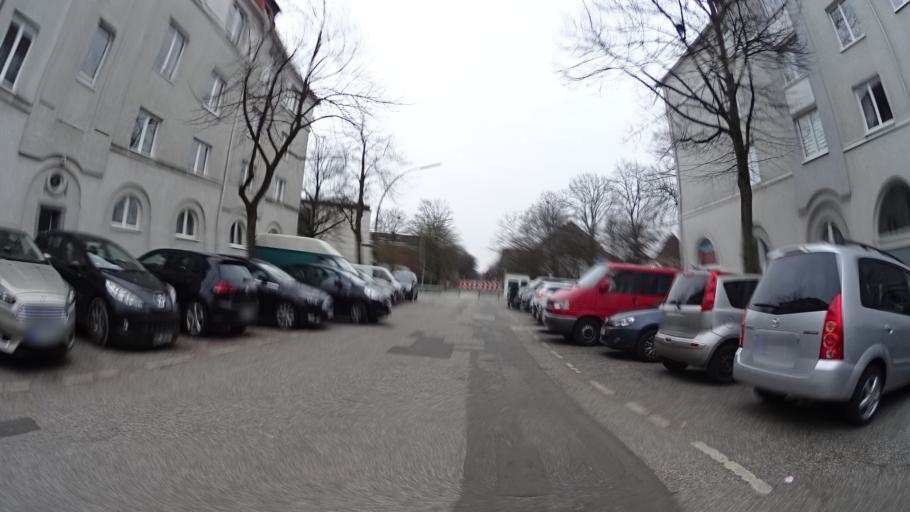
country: DE
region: Hamburg
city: Eimsbuettel
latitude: 53.5738
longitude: 9.9697
